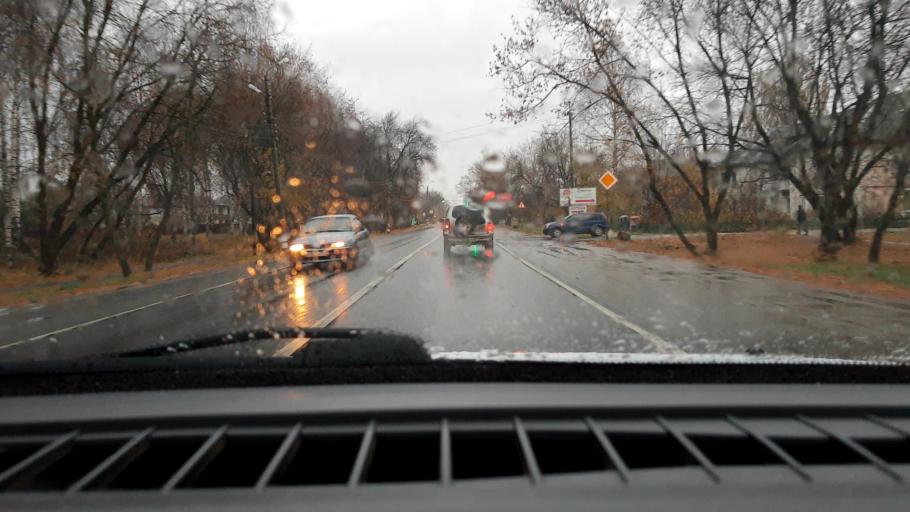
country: RU
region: Nizjnij Novgorod
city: Neklyudovo
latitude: 56.3984
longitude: 44.0082
